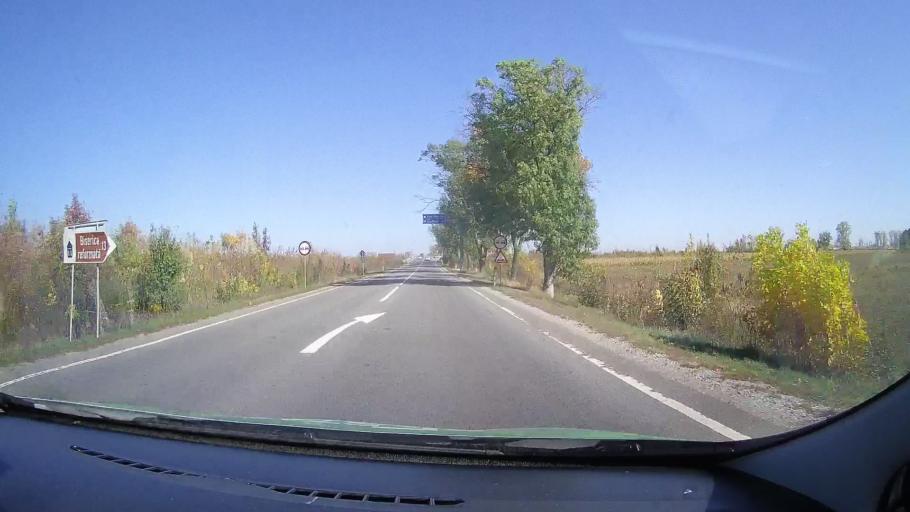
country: RO
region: Satu Mare
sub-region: Comuna Moftinu
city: Moftinu Mic
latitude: 47.7044
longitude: 22.6332
